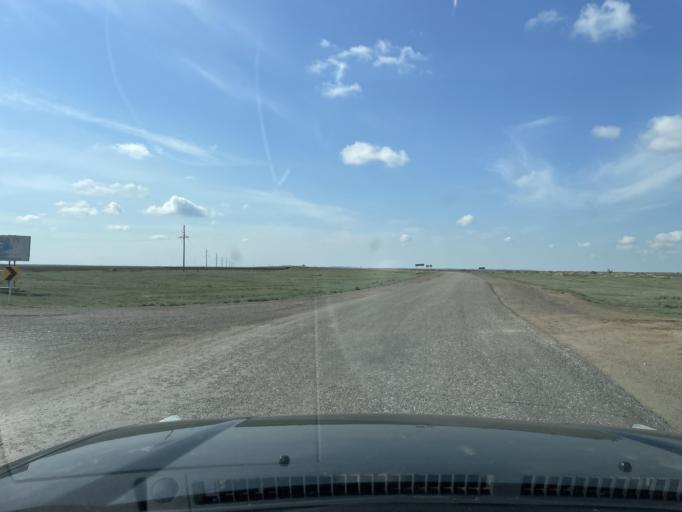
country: KZ
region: Qaraghandy
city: Zhezqazghan
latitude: 47.6689
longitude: 67.8480
